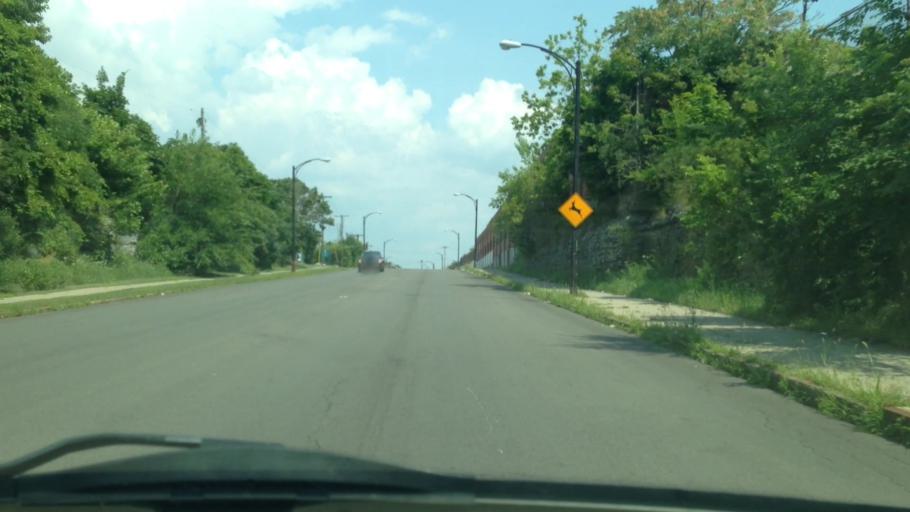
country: US
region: New York
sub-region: Erie County
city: Eggertsville
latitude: 42.9401
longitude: -78.8264
